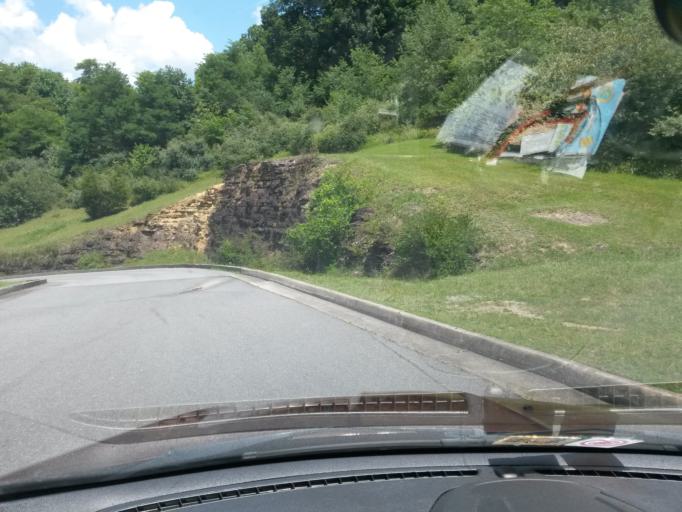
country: US
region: West Virginia
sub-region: Wyoming County
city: Mullens
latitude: 37.6415
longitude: -81.4546
